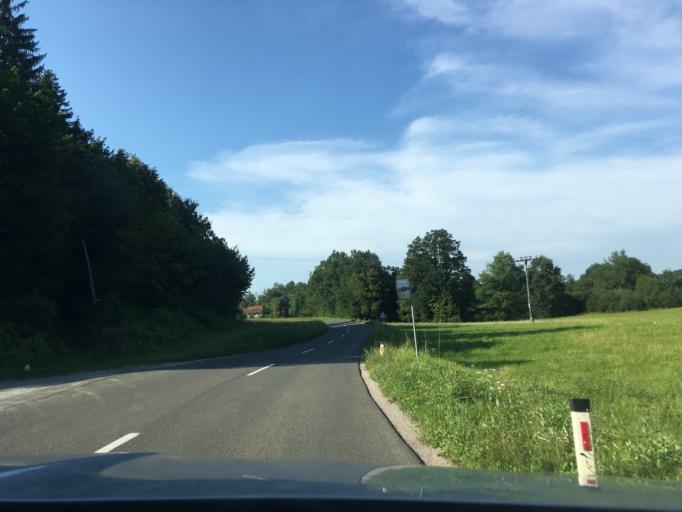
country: SI
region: Crnomelj
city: Crnomelj
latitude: 45.5037
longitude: 15.1898
